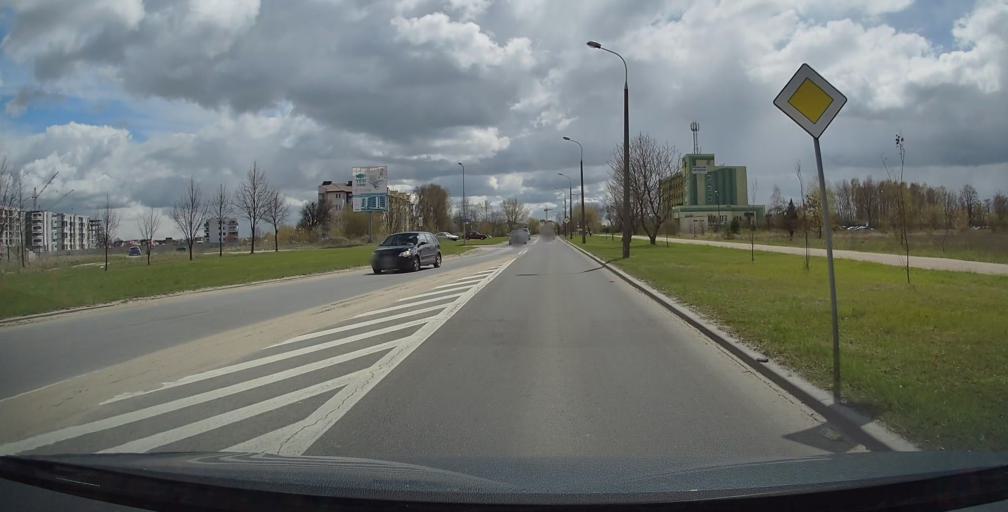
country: PL
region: Masovian Voivodeship
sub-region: Ostroleka
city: Ostroleka
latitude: 53.0670
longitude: 21.5915
